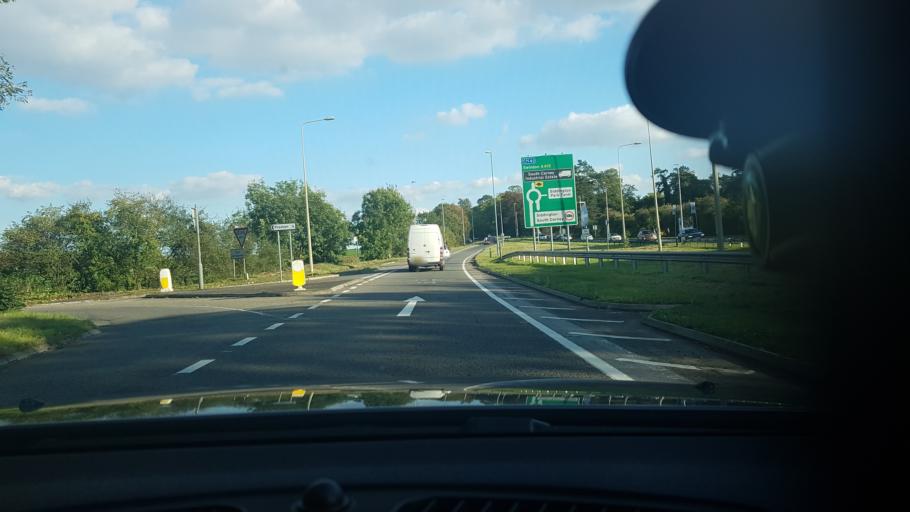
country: GB
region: England
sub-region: Gloucestershire
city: Cirencester
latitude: 51.7041
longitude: -1.9454
